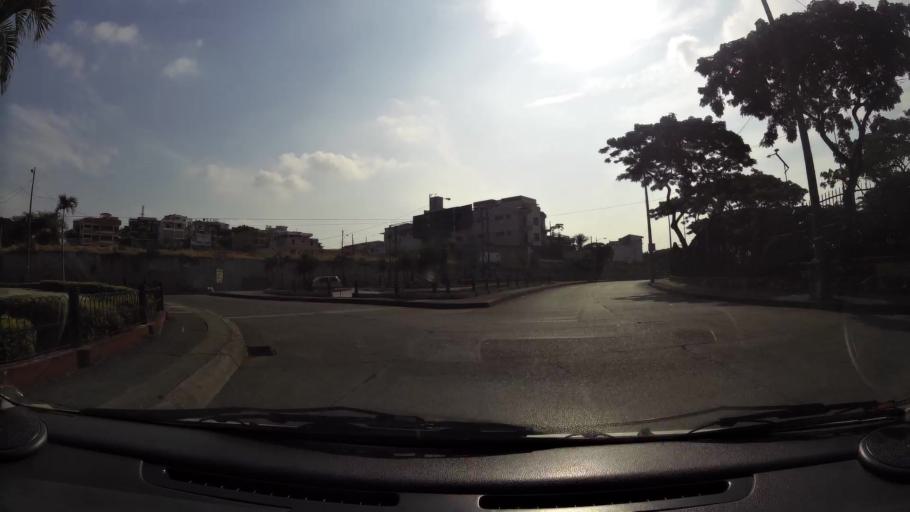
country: EC
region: Guayas
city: Guayaquil
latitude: -2.1861
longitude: -79.9028
